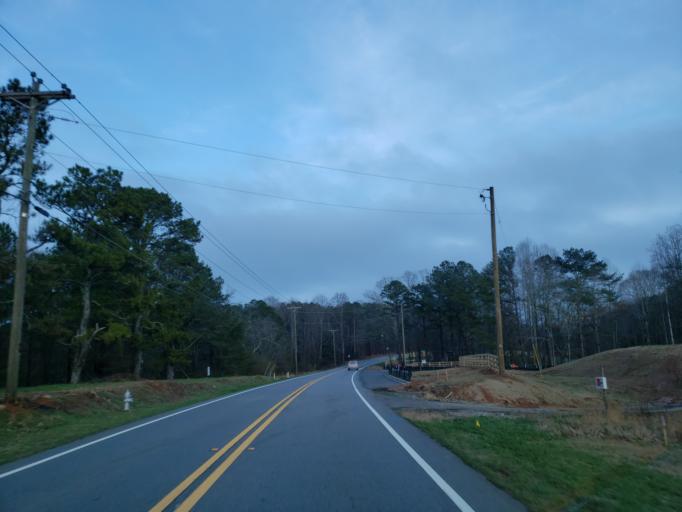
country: US
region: Georgia
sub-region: Cherokee County
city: Ball Ground
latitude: 34.2395
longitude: -84.3402
